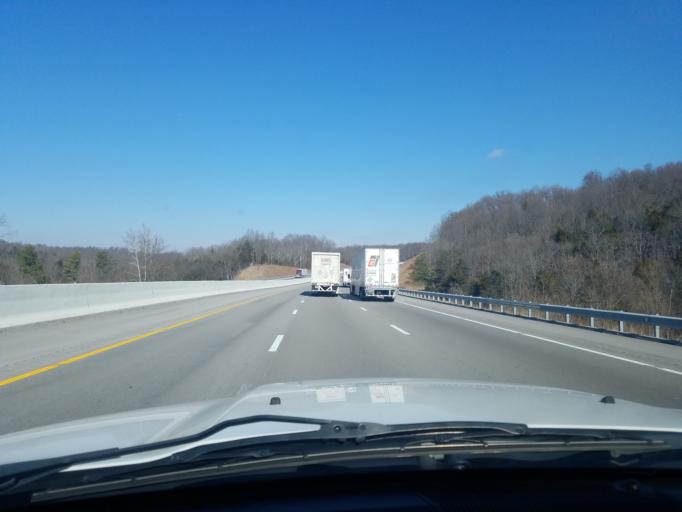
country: US
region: Kentucky
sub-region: Hart County
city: Munfordville
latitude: 37.3332
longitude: -85.9072
